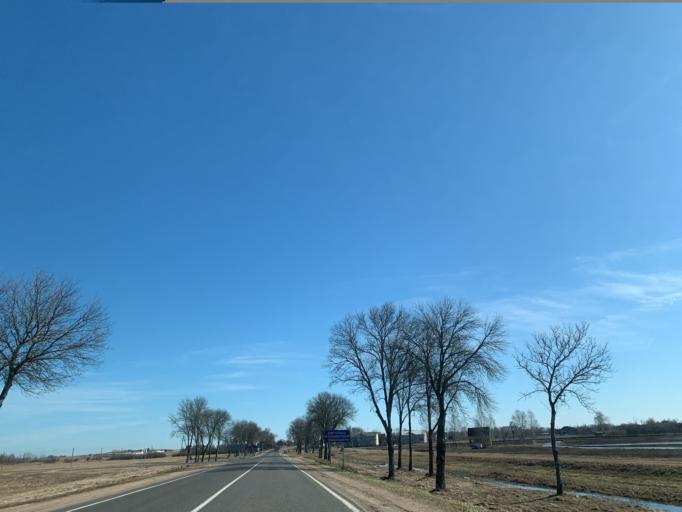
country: BY
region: Minsk
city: Nyasvizh
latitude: 53.2288
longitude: 26.7222
